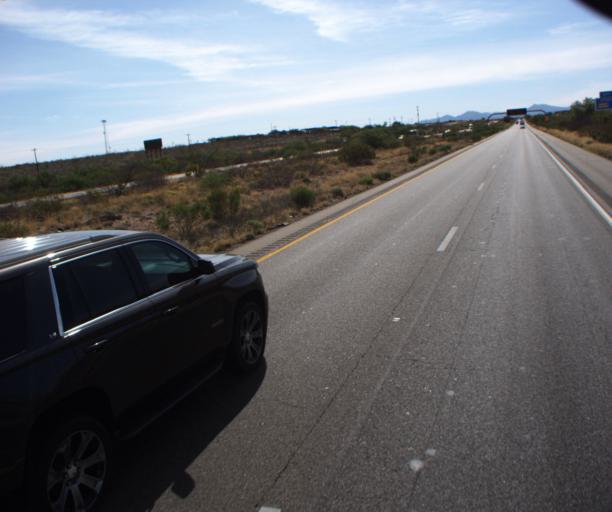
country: US
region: Arizona
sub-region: Pima County
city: Vail
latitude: 32.0164
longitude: -110.7047
